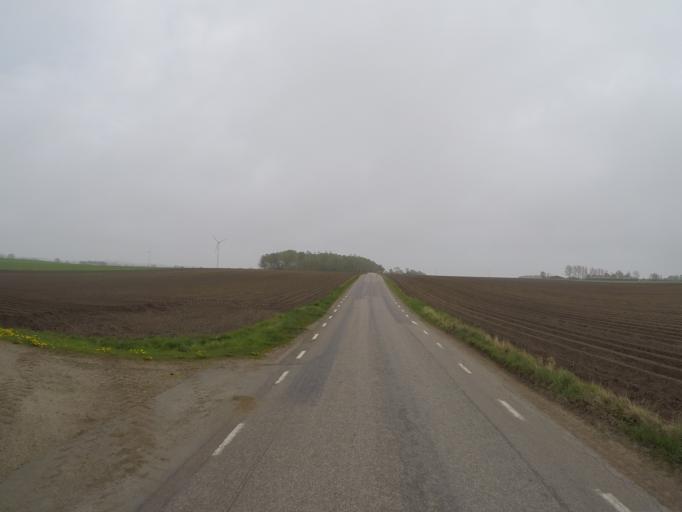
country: SE
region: Halland
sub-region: Laholms Kommun
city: Mellbystrand
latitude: 56.5272
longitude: 12.9841
